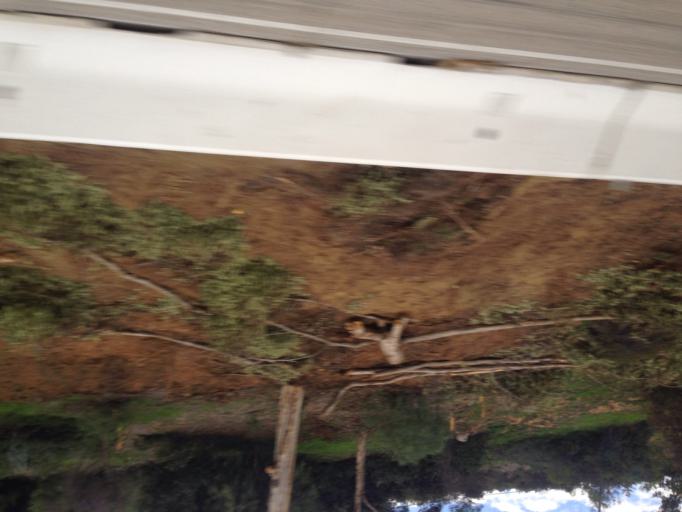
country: US
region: California
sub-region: San Diego County
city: National City
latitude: 32.6706
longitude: -117.0815
